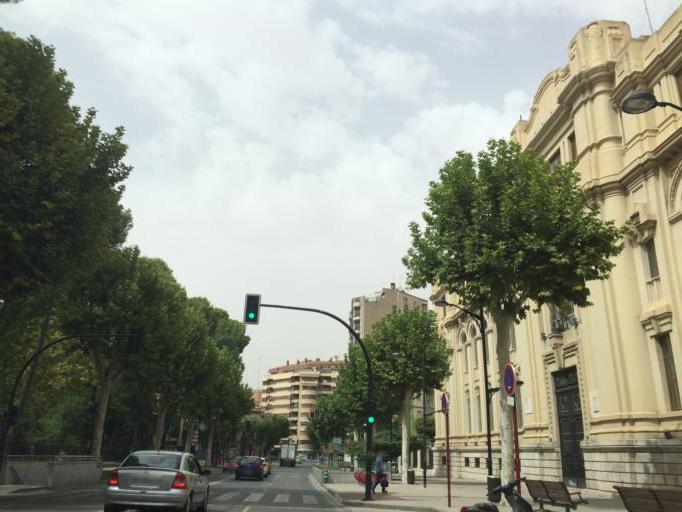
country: ES
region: Castille-La Mancha
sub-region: Provincia de Albacete
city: Albacete
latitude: 38.9889
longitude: -1.8556
